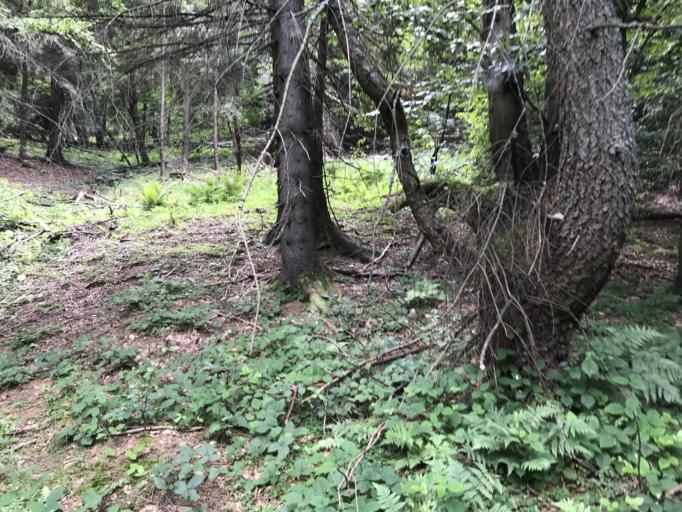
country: PL
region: Lesser Poland Voivodeship
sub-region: Powiat gorlicki
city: Uscie Gorlickie
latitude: 49.4510
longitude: 21.2208
